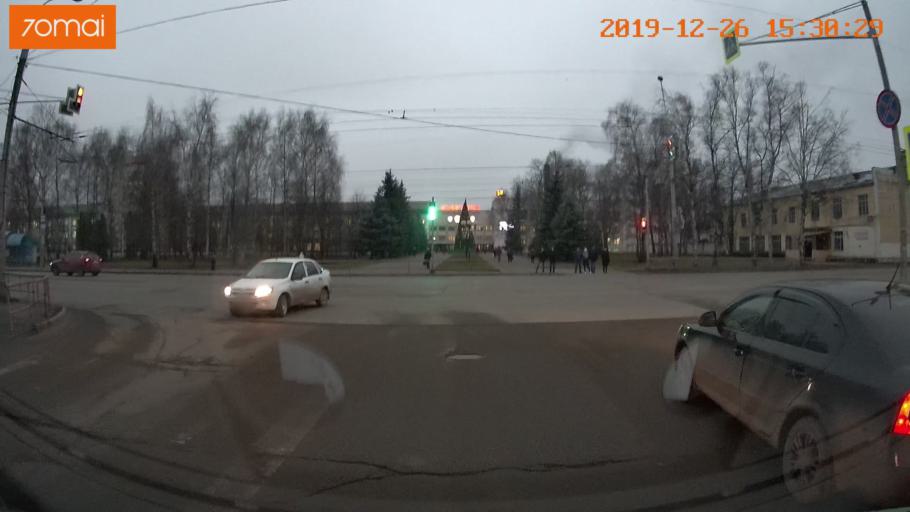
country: RU
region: Jaroslavl
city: Rybinsk
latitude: 58.0553
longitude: 38.8164
